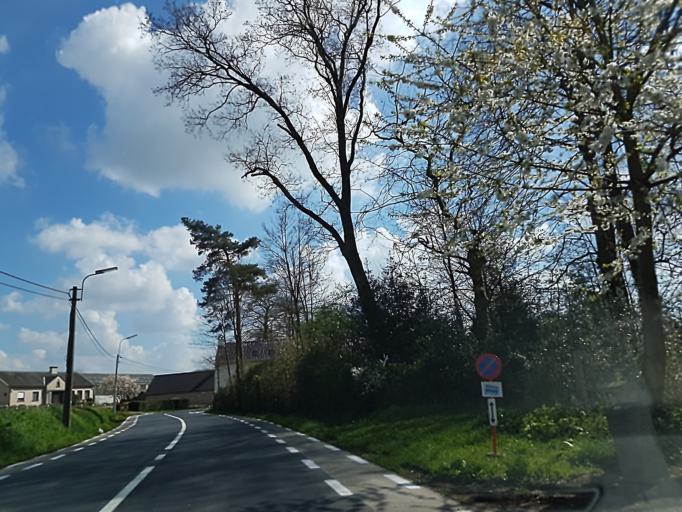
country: BE
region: Flanders
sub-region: Provincie Oost-Vlaanderen
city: Sint-Maria-Lierde
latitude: 50.8336
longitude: 3.8724
